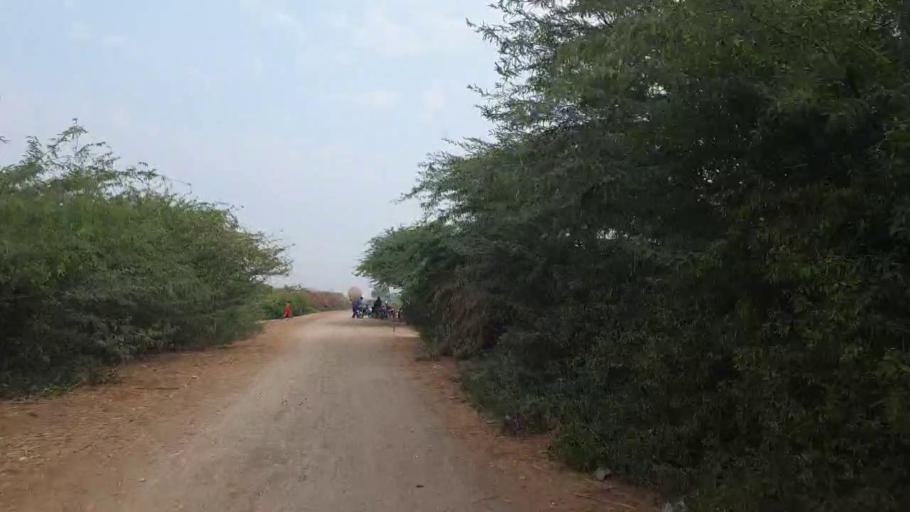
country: PK
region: Sindh
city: Tando Bago
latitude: 24.7953
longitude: 68.8761
